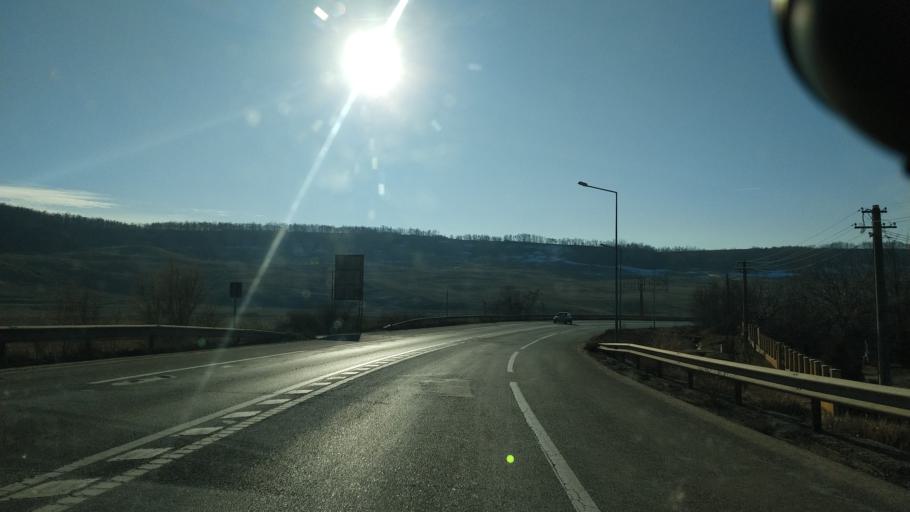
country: RO
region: Iasi
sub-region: Comuna Targu Frumos
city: Targu Frumos
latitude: 47.1964
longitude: 26.9979
